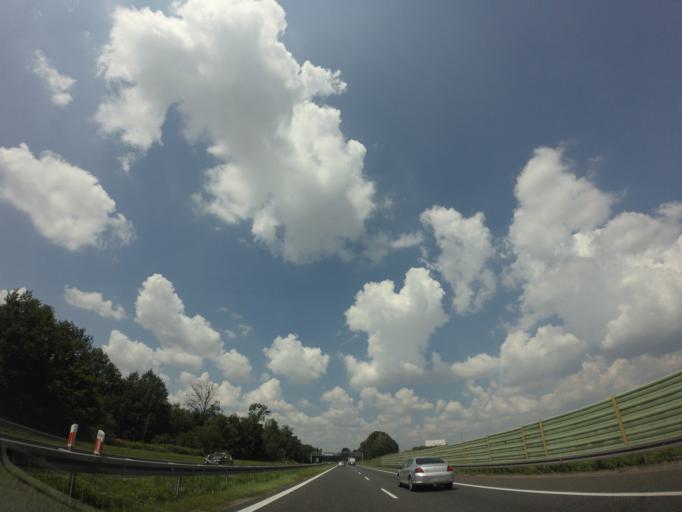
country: PL
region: Opole Voivodeship
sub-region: Powiat strzelecki
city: Ujazd
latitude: 50.4365
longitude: 18.3650
